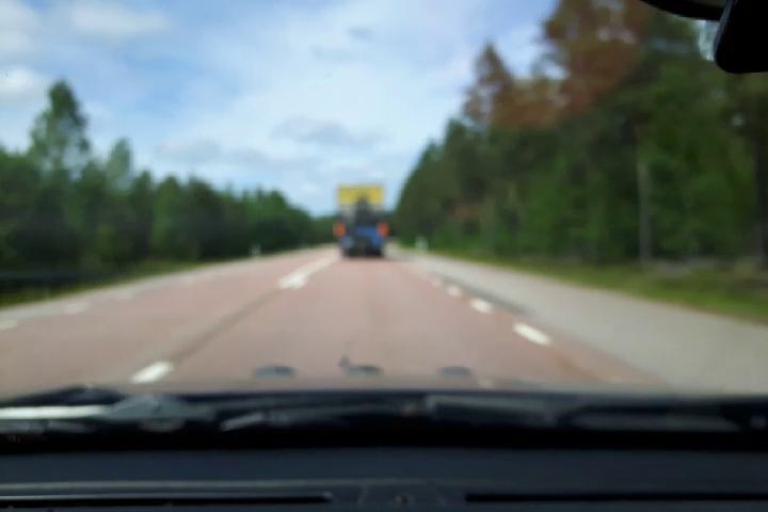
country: SE
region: Uppsala
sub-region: Osthammars Kommun
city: Bjorklinge
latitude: 60.1785
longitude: 17.4818
